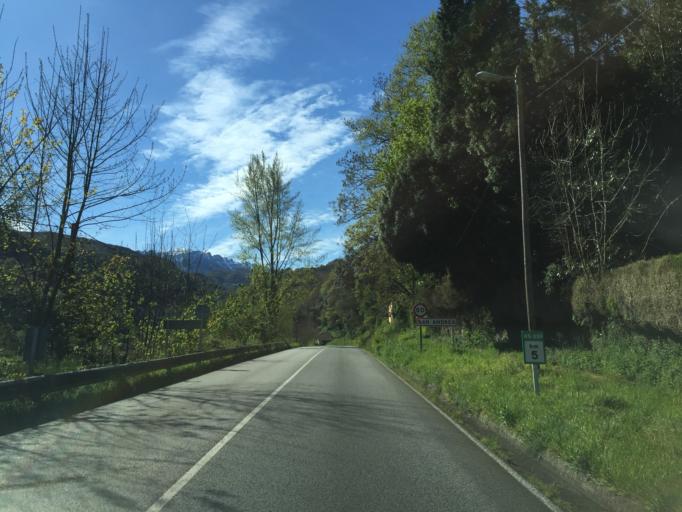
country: ES
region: Asturias
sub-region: Province of Asturias
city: Proaza
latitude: 43.3178
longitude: -5.9918
